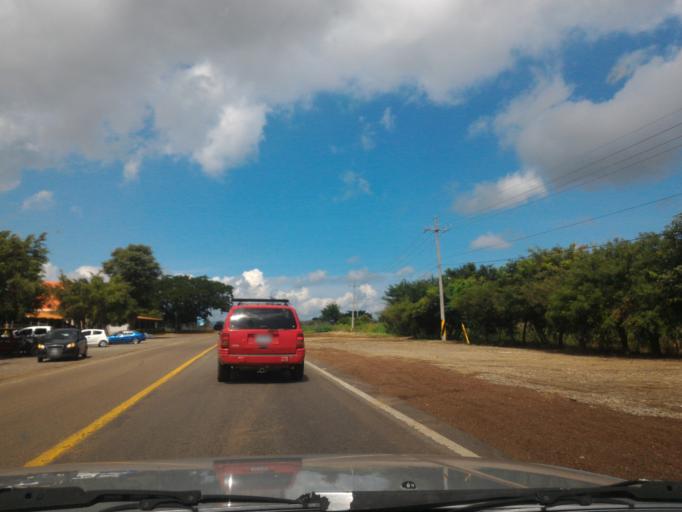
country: MX
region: Jalisco
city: Amatitan
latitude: 20.8560
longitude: -103.7640
